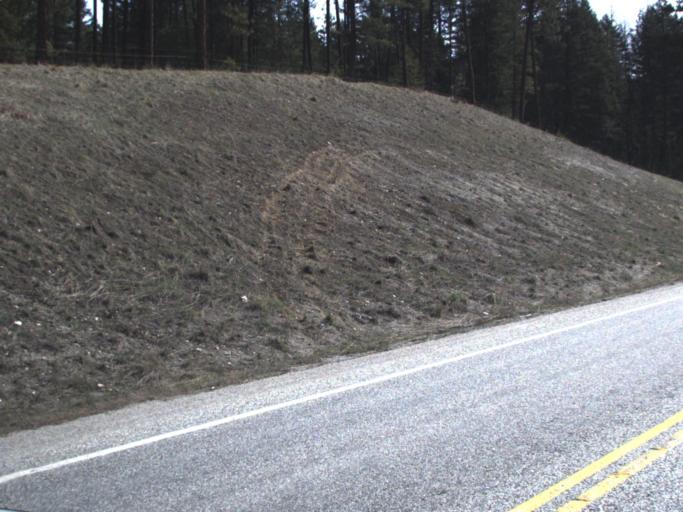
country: US
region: Washington
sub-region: Stevens County
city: Colville
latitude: 48.5405
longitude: -117.8392
